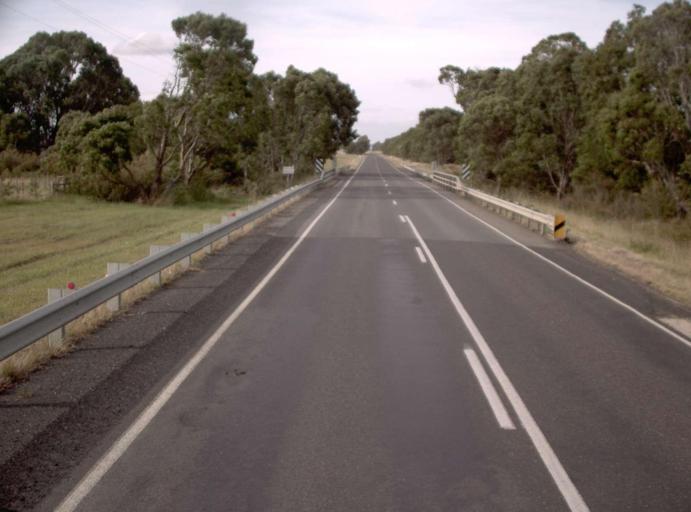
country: AU
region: Victoria
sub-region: Wellington
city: Heyfield
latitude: -38.0492
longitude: 146.6641
